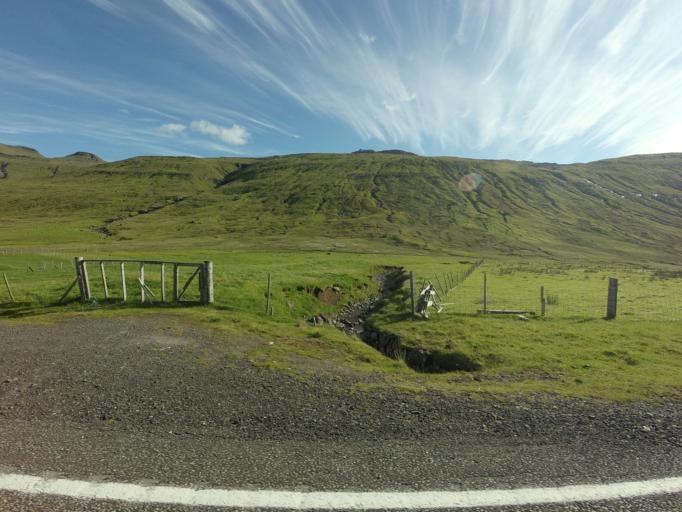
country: FO
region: Streymoy
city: Kollafjordhur
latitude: 62.1203
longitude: -6.9858
